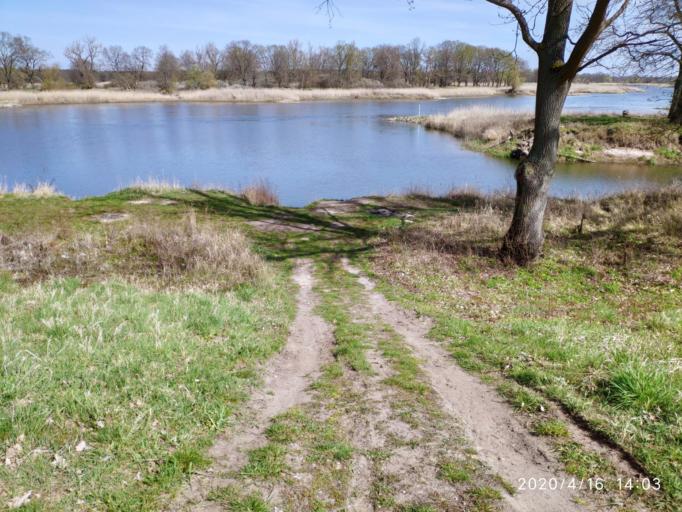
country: PL
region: Lubusz
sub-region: Powiat krosnienski
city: Dabie
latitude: 52.0676
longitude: 15.2556
